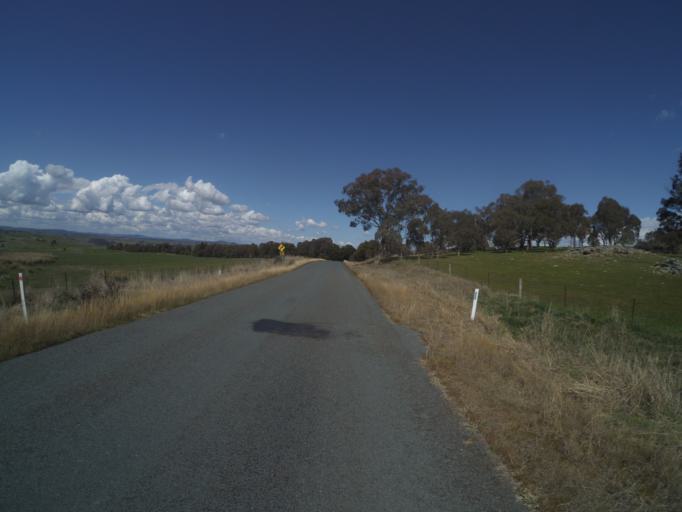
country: AU
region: Australian Capital Territory
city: Macquarie
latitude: -35.2129
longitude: 148.9101
